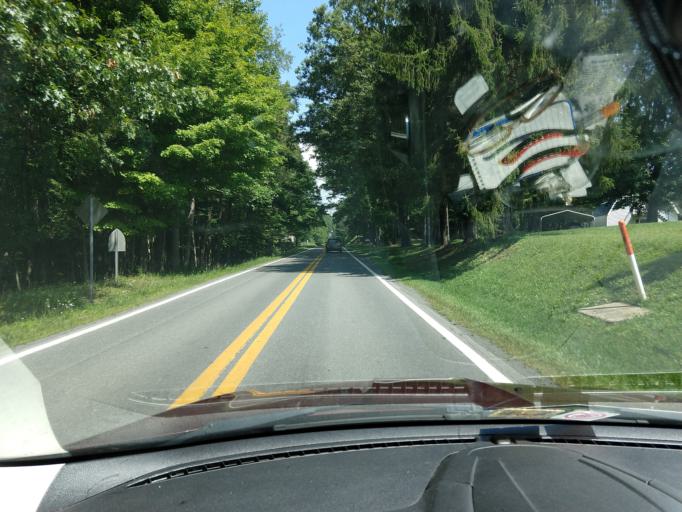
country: US
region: West Virginia
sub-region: Greenbrier County
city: Fairlea
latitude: 37.8257
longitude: -80.5591
